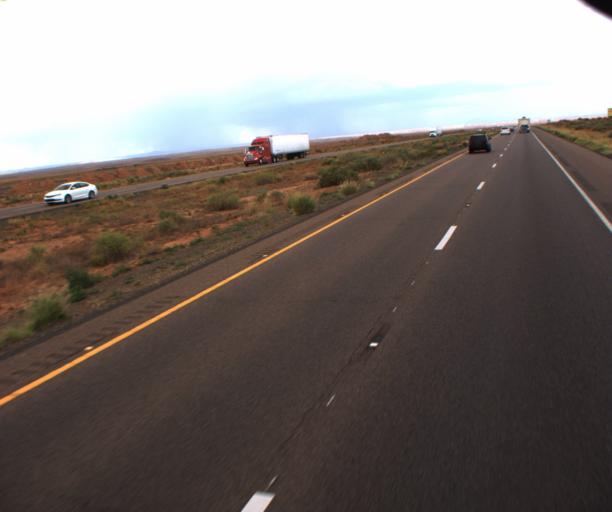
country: US
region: Arizona
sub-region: Coconino County
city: LeChee
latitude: 35.0748
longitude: -110.8601
